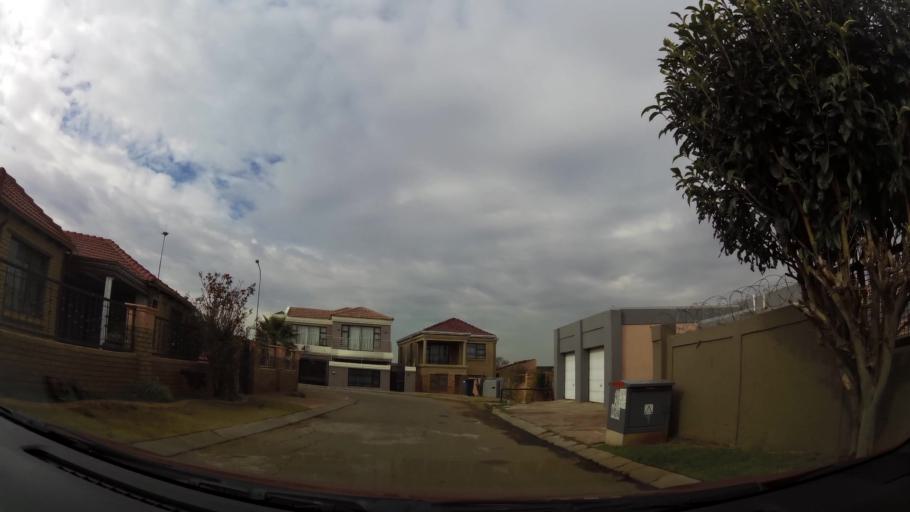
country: ZA
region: Gauteng
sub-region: City of Johannesburg Metropolitan Municipality
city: Soweto
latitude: -26.2772
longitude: 27.8315
